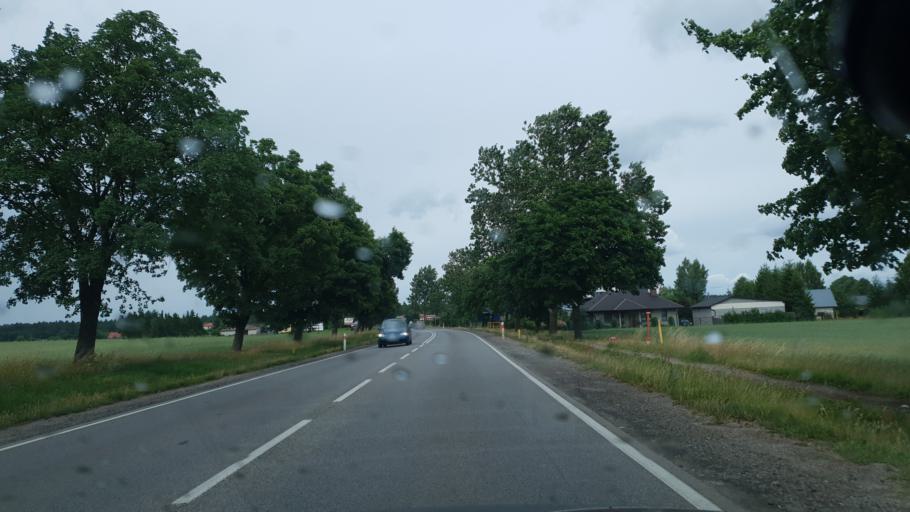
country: PL
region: Pomeranian Voivodeship
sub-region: Powiat kartuski
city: Banino
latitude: 54.4241
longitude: 18.3845
